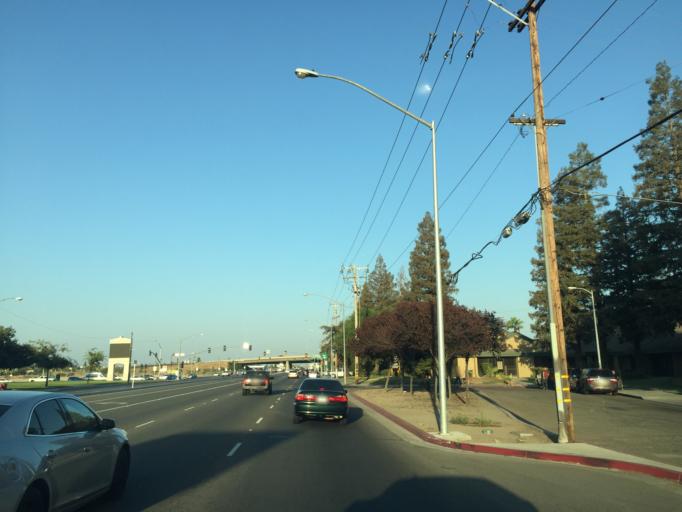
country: US
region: California
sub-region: Fresno County
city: Clovis
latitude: 36.8085
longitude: -119.7383
